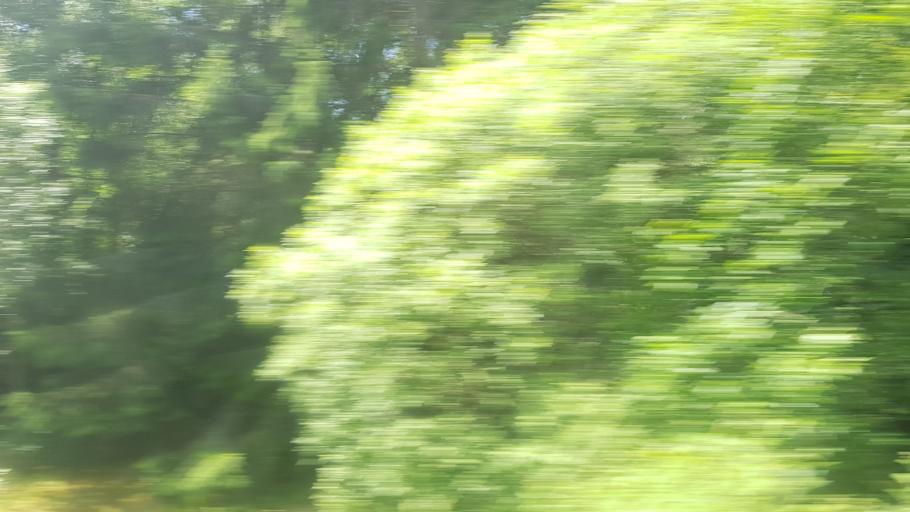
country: SE
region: Vaestra Goetaland
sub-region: Kungalvs Kommun
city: Kode
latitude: 57.9669
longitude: 11.8377
